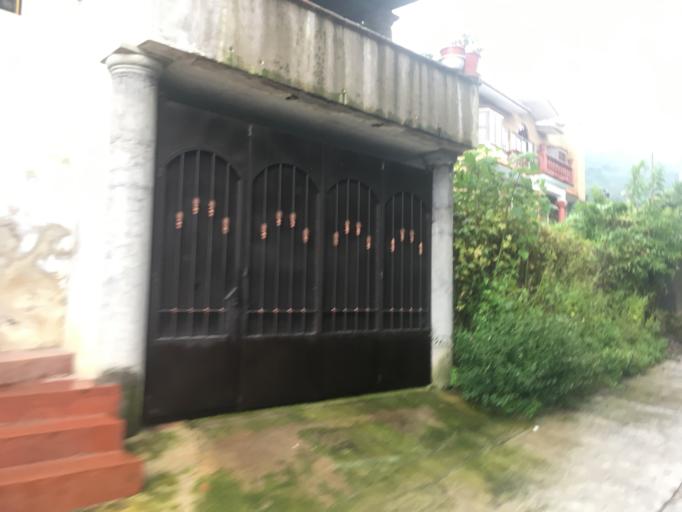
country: MX
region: Morelos
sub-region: Tlayacapan
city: Tlayacapan
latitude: 18.9530
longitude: -98.9906
